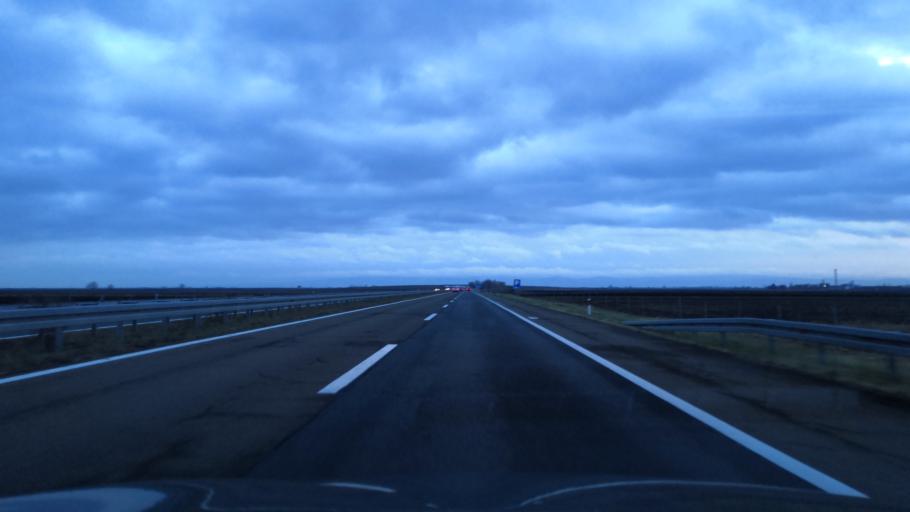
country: RS
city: Kisac
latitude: 45.3726
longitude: 19.7490
